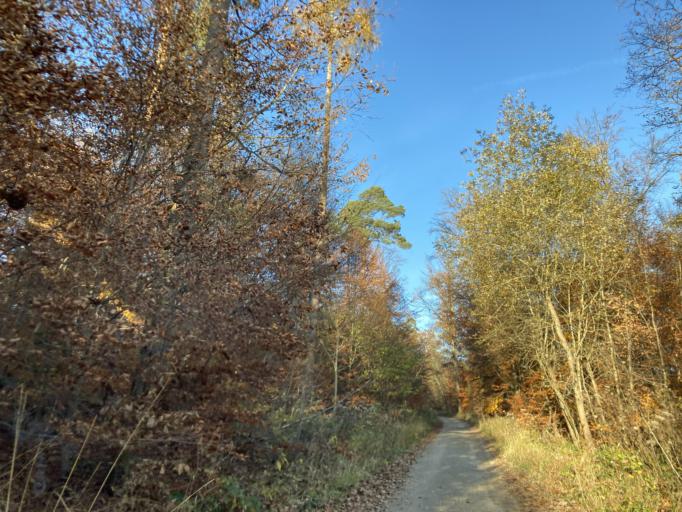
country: DE
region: Baden-Wuerttemberg
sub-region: Tuebingen Region
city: Tuebingen
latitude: 48.5468
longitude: 8.9847
